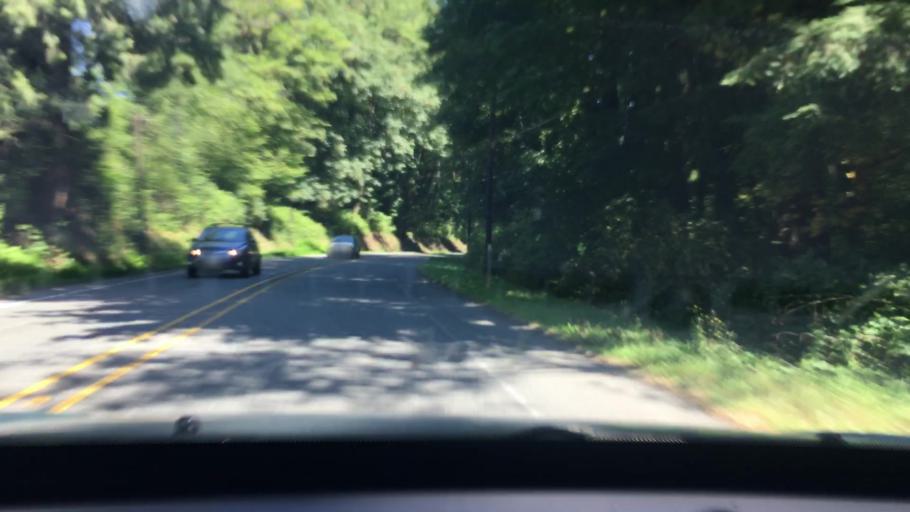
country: US
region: Washington
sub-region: King County
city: Issaquah
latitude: 47.5234
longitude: -122.0675
